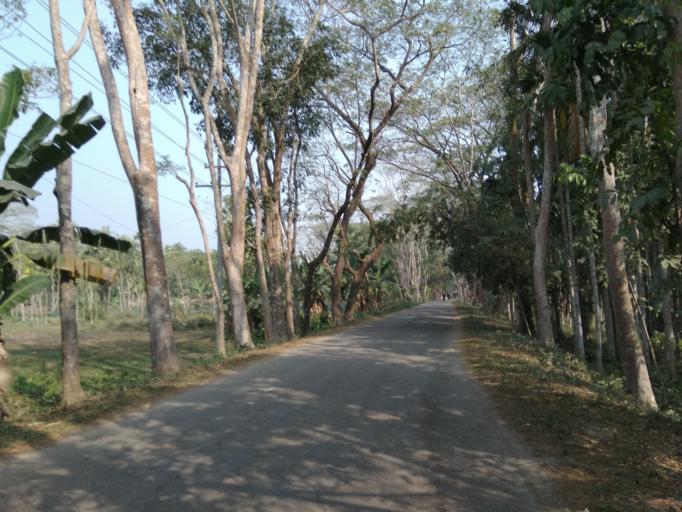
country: BD
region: Barisal
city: Mehendiganj
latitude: 22.9623
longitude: 90.4145
